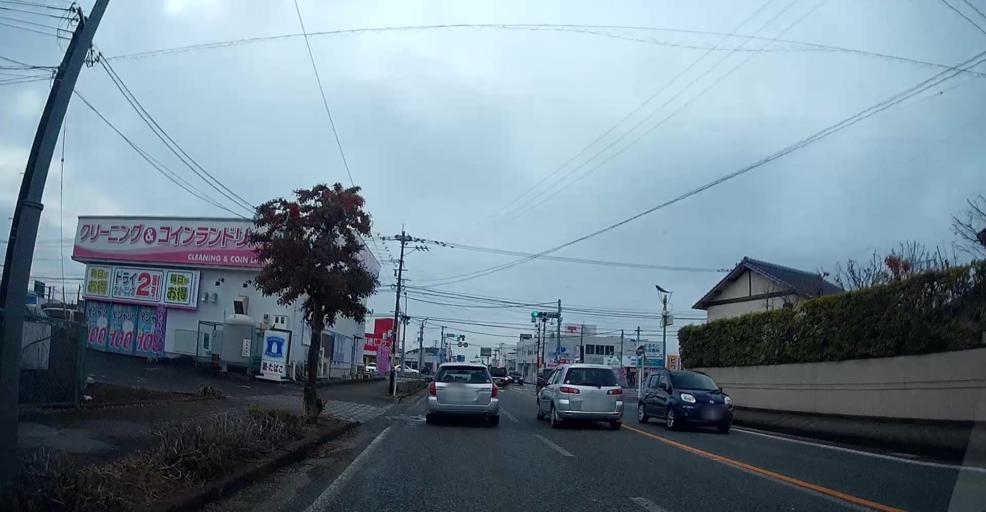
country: JP
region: Kumamoto
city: Matsubase
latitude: 32.6527
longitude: 130.6766
